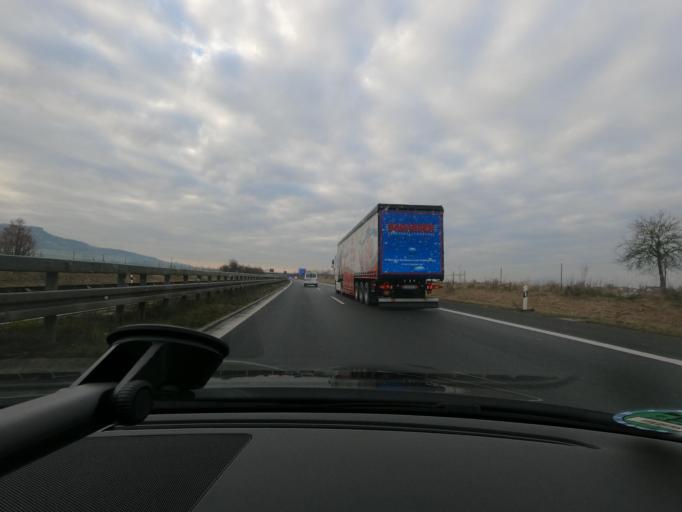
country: DE
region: Bavaria
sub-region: Upper Franconia
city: Bad Staffelstein
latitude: 50.1191
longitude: 11.0210
